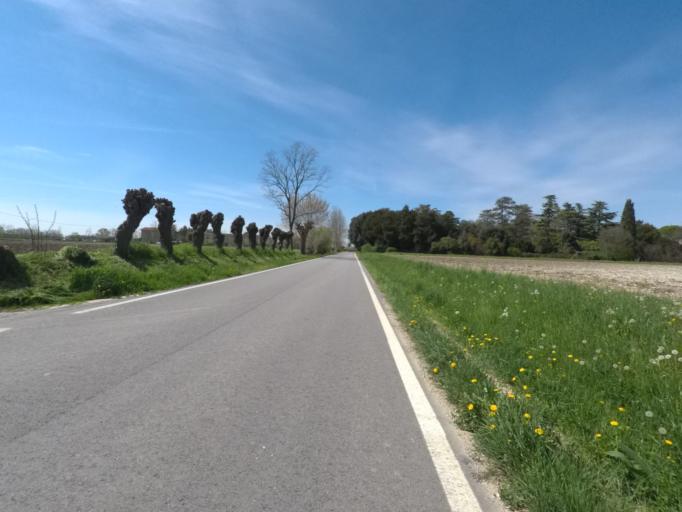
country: IT
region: Friuli Venezia Giulia
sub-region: Provincia di Udine
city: Codroipo
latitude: 45.9560
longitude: 12.9565
